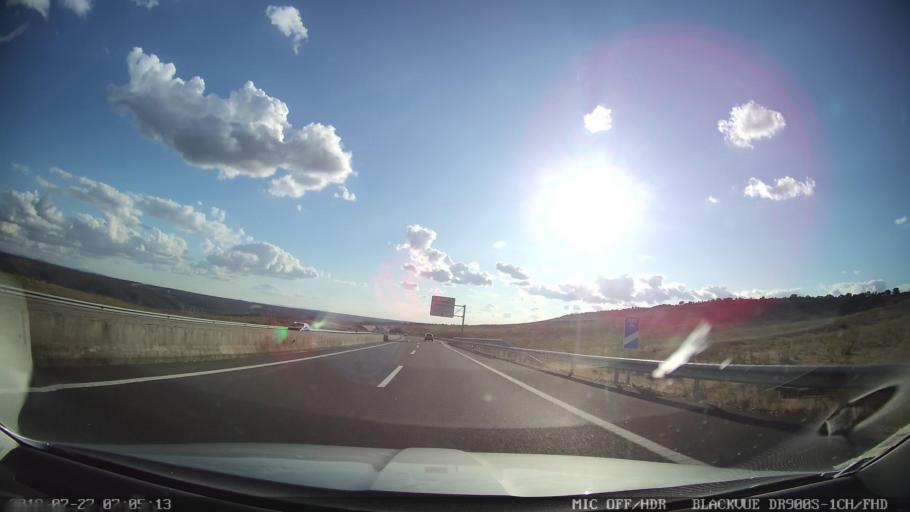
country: ES
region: Extremadura
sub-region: Provincia de Caceres
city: Jaraicejo
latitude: 39.6621
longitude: -5.7850
